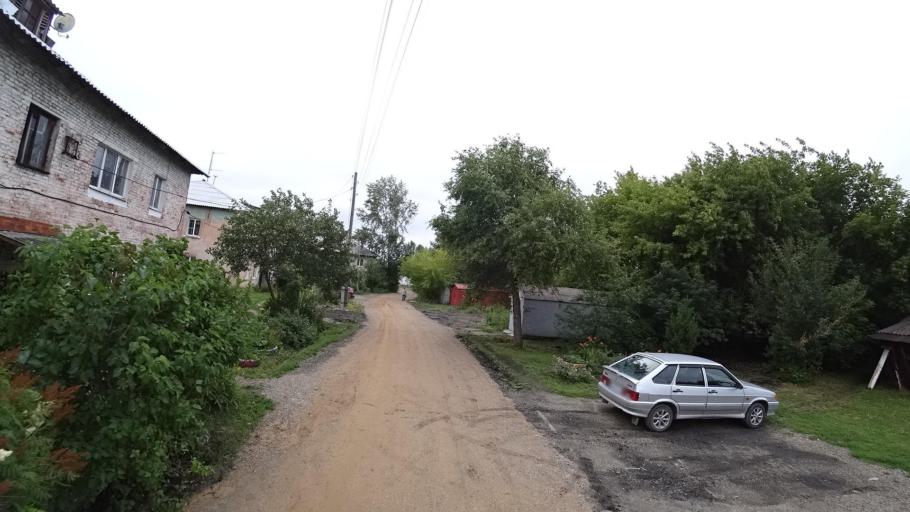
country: RU
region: Sverdlovsk
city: Kamyshlov
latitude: 56.8422
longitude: 62.7433
